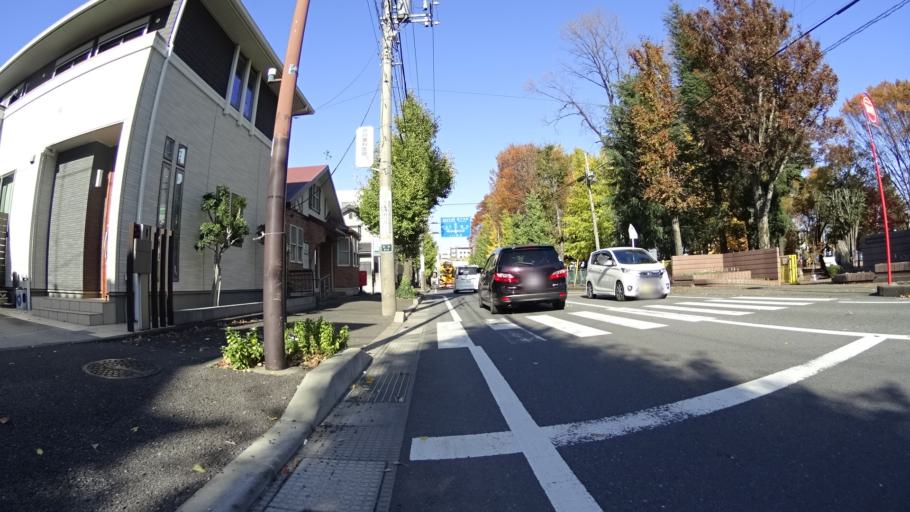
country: JP
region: Tokyo
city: Hachioji
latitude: 35.5779
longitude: 139.3609
